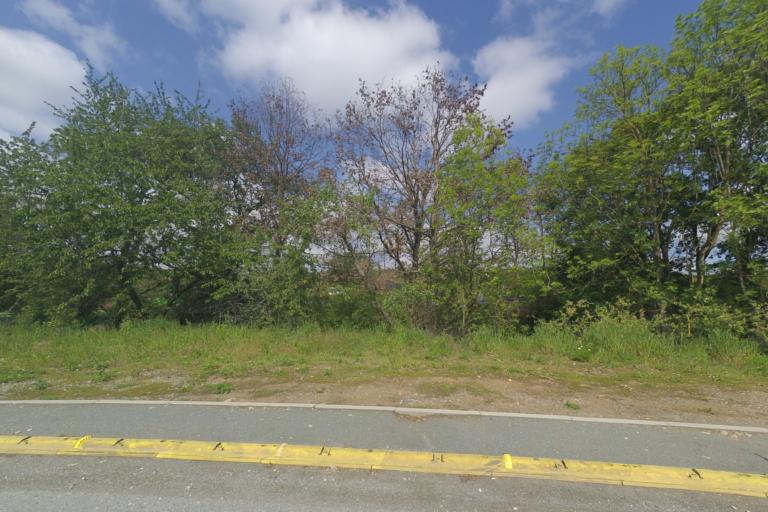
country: DE
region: Hesse
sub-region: Regierungsbezirk Darmstadt
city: Rosbach vor der Hohe
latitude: 50.2966
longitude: 8.6824
